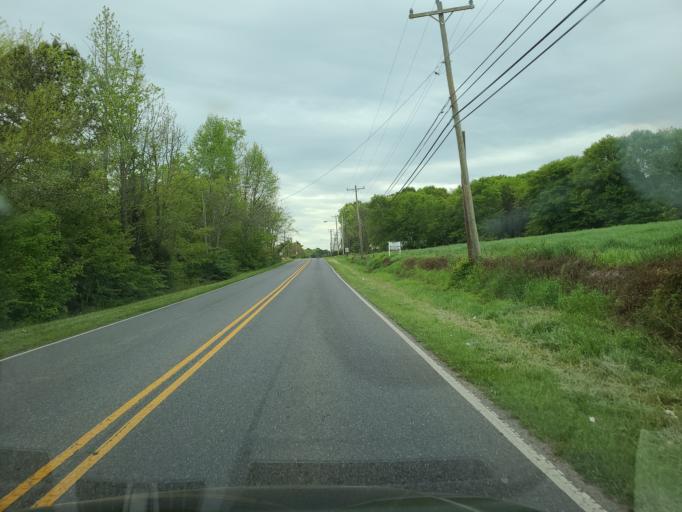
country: US
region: North Carolina
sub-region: Cleveland County
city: Shelby
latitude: 35.2995
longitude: -81.5083
